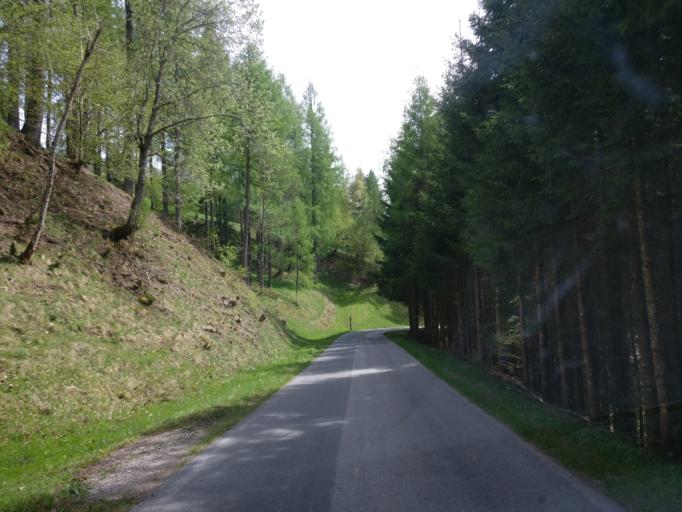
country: AT
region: Salzburg
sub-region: Politischer Bezirk Sankt Johann im Pongau
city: Pfarrwerfen
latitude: 47.4802
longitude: 13.2089
